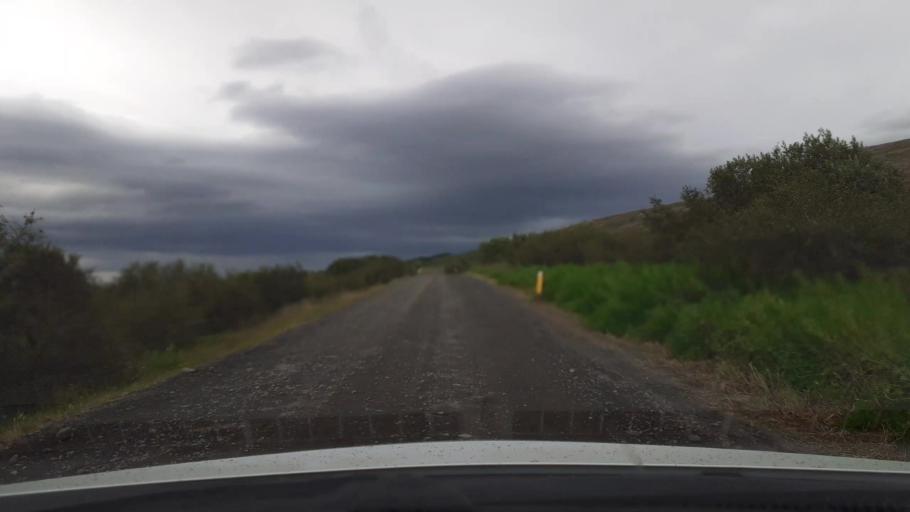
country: IS
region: Capital Region
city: Mosfellsbaer
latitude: 64.5251
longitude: -21.4785
